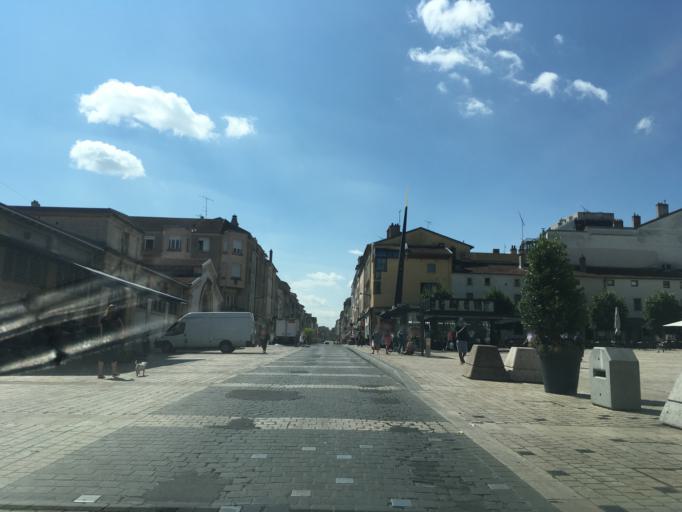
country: FR
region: Lorraine
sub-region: Departement de Meurthe-et-Moselle
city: Nancy
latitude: 48.6893
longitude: 6.1821
